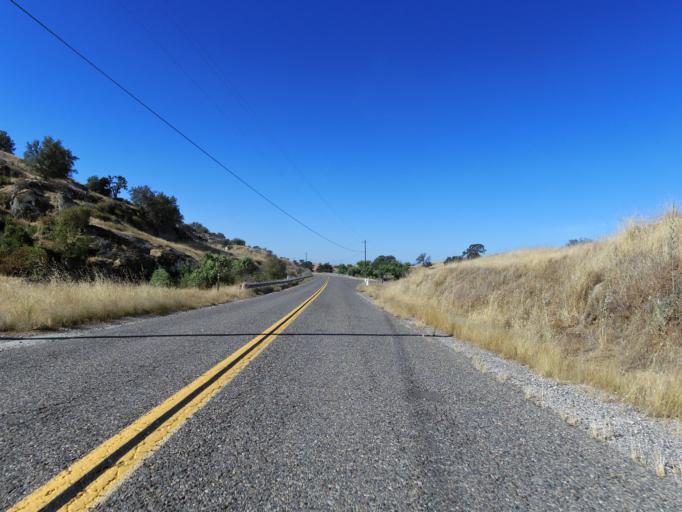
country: US
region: California
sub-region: Madera County
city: Yosemite Lakes
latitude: 37.1162
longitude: -119.8662
